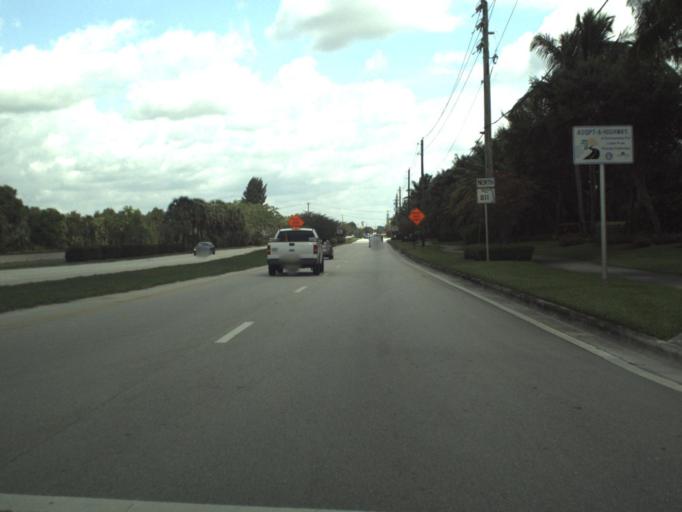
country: US
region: Florida
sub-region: Palm Beach County
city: North Palm Beach
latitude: 26.8308
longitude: -80.0916
